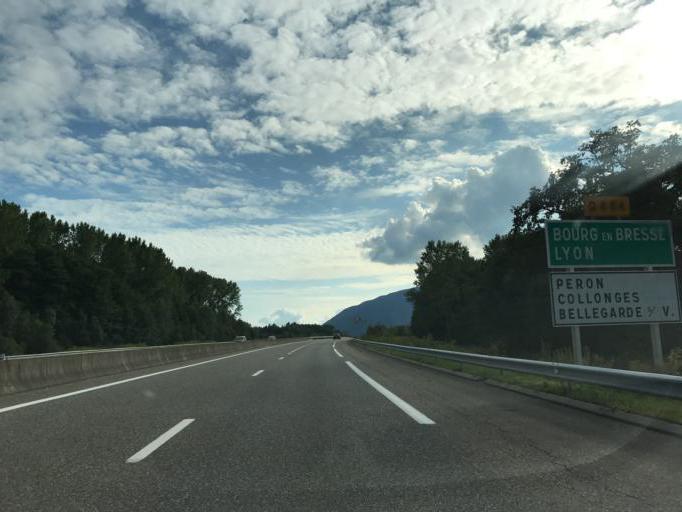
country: FR
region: Rhone-Alpes
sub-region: Departement de l'Ain
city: Challex
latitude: 46.1951
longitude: 5.9616
